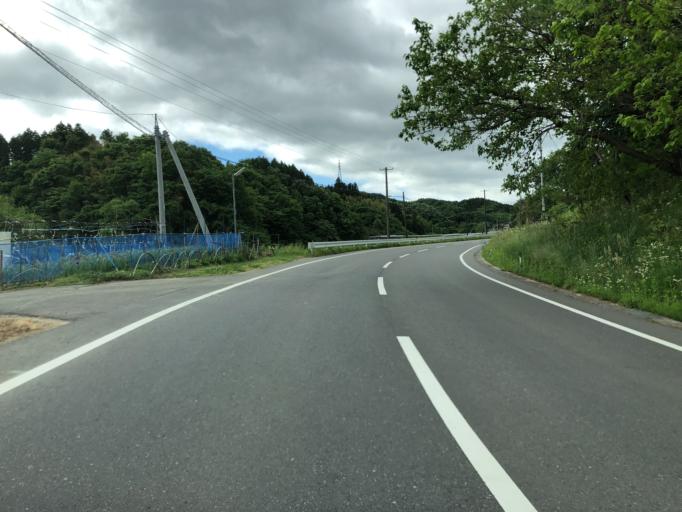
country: JP
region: Fukushima
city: Nihommatsu
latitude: 37.5467
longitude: 140.4602
